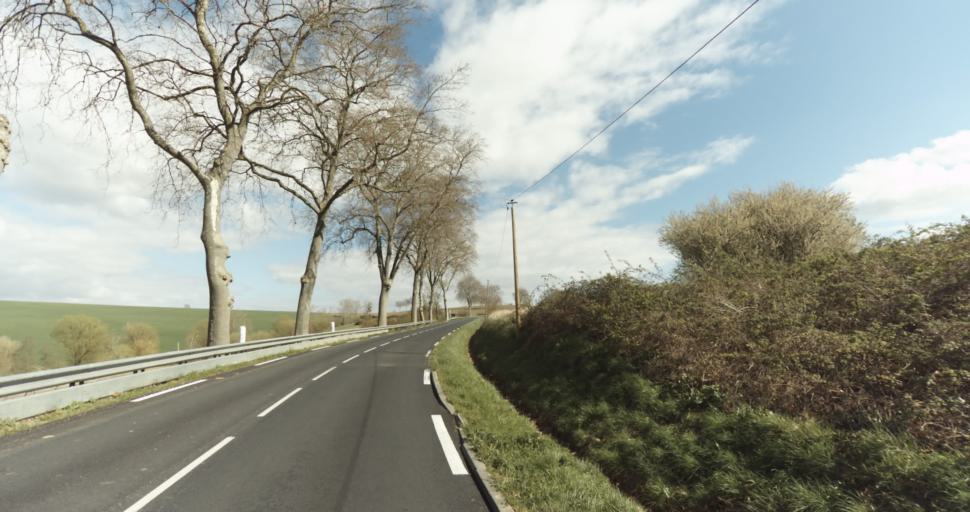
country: FR
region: Midi-Pyrenees
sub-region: Departement de la Haute-Garonne
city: Auterive
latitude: 43.3587
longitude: 1.4873
